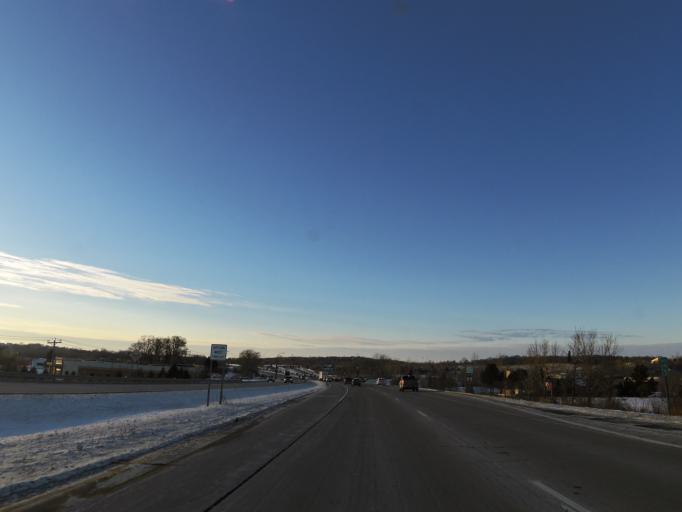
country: US
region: Minnesota
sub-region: Carver County
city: Chanhassen
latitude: 44.8607
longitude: -93.5446
